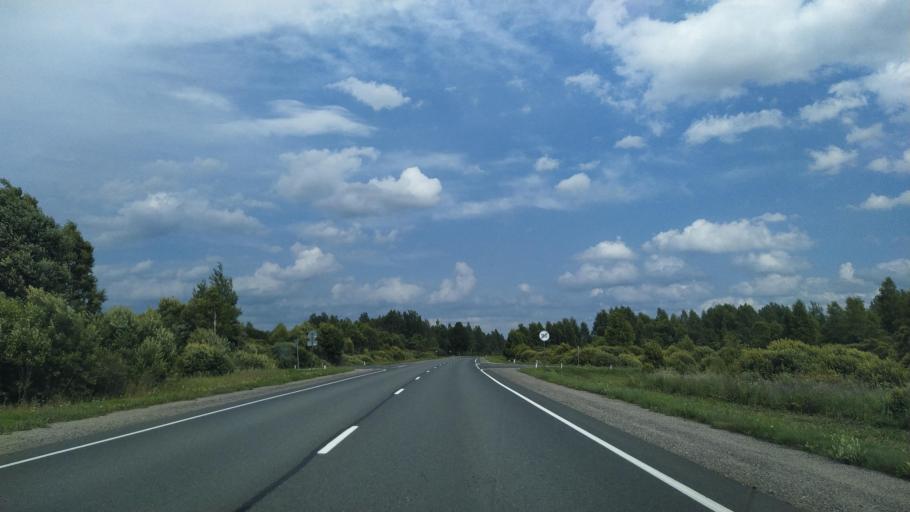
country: RU
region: Pskov
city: Porkhov
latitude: 57.9765
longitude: 29.7091
